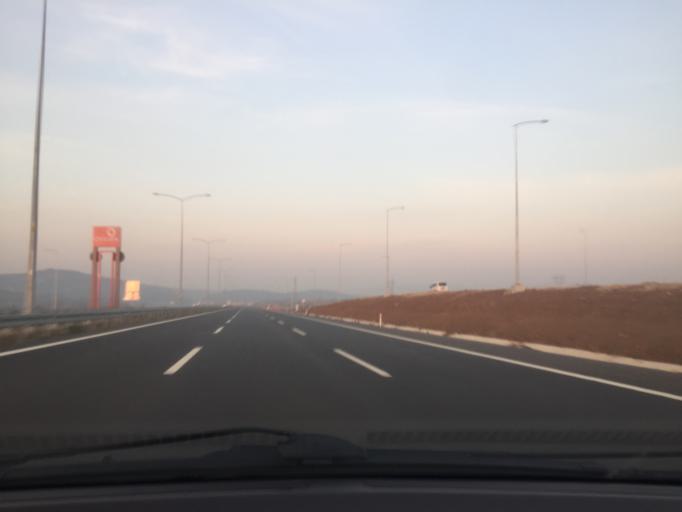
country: TR
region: Bursa
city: Mahmudiye
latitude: 40.2731
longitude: 28.5985
